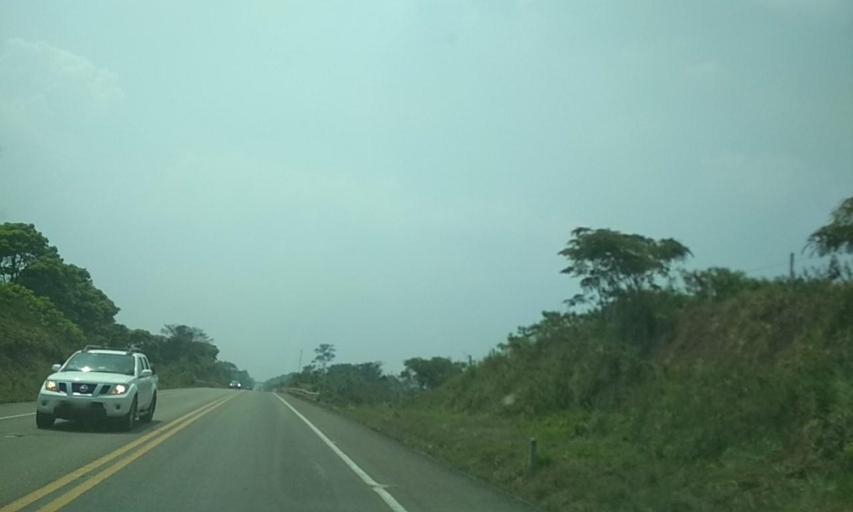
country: MX
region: Tabasco
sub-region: Huimanguillo
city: Francisco Rueda
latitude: 17.7414
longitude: -93.9825
